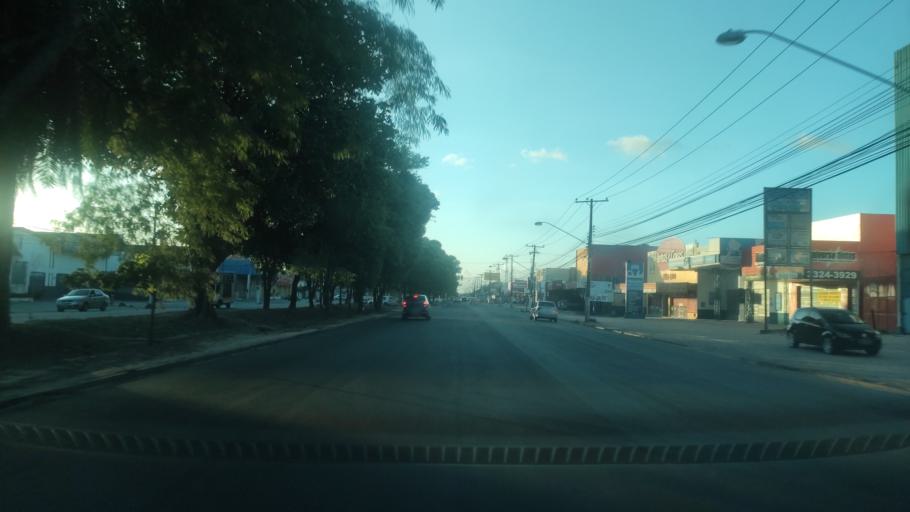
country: BR
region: Alagoas
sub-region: Satuba
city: Satuba
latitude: -9.5877
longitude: -35.7620
